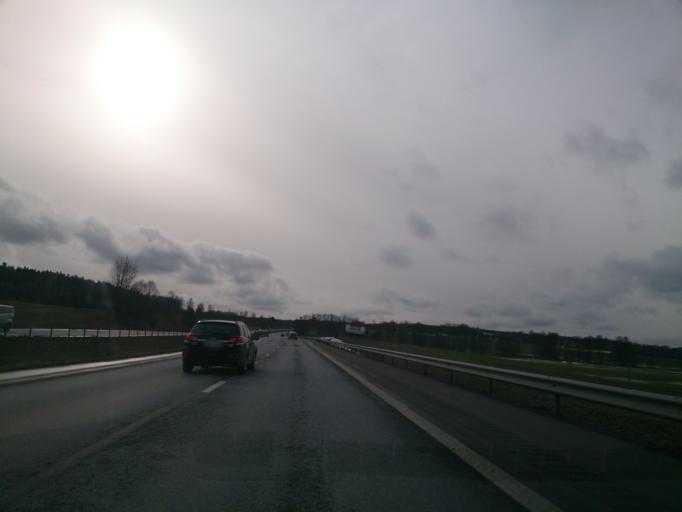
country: SE
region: Soedermanland
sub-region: Trosa Kommun
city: Vagnharad
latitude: 58.9473
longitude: 17.4337
